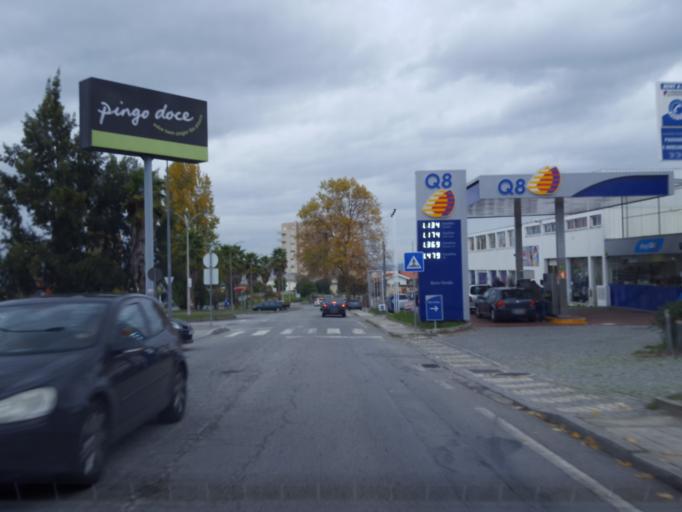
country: PT
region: Porto
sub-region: Marco de Canaveses
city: Marco de Canavezes
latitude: 41.1773
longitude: -8.1509
